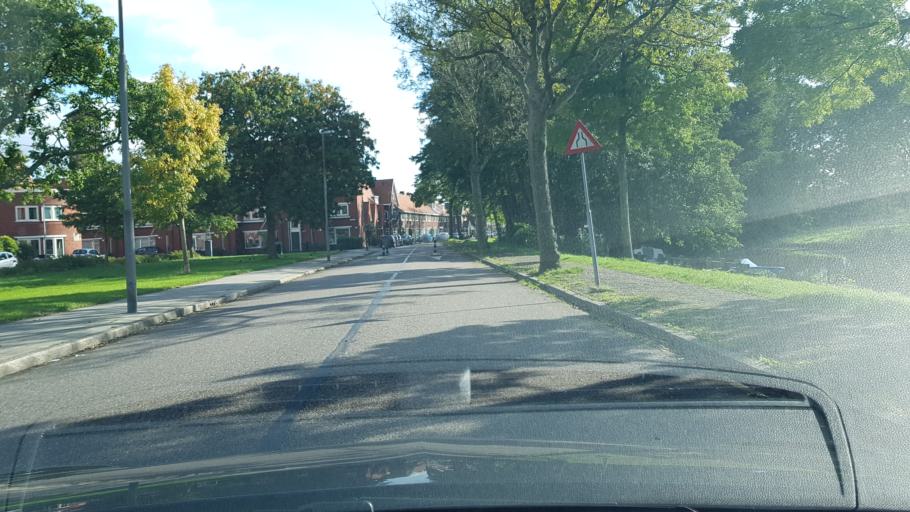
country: NL
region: North Holland
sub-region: Gemeente Bloemendaal
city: Bloemendaal
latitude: 52.4125
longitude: 4.6474
